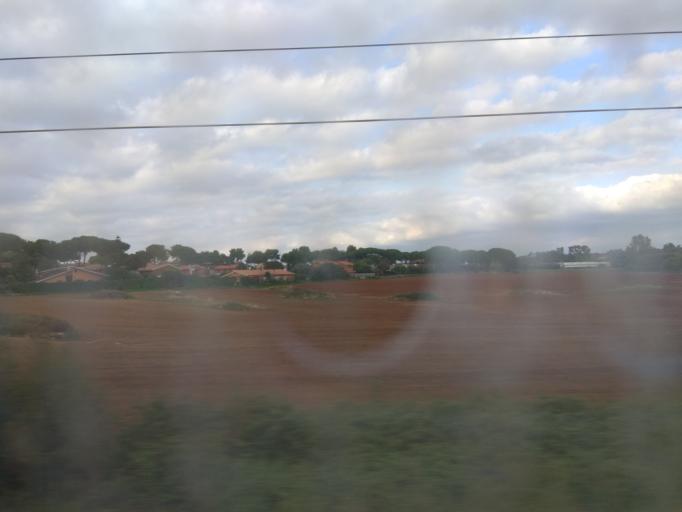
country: IT
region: Latium
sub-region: Citta metropolitana di Roma Capitale
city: Marina San Nicola
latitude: 41.9327
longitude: 12.1355
